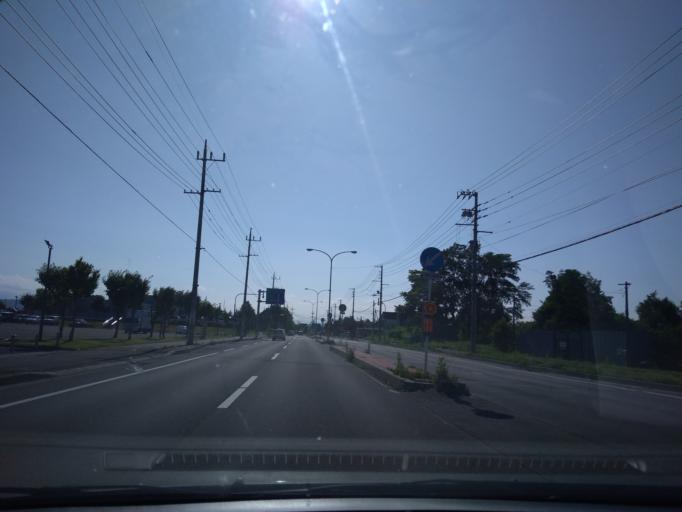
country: JP
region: Hokkaido
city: Kitahiroshima
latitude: 42.9797
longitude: 141.4897
